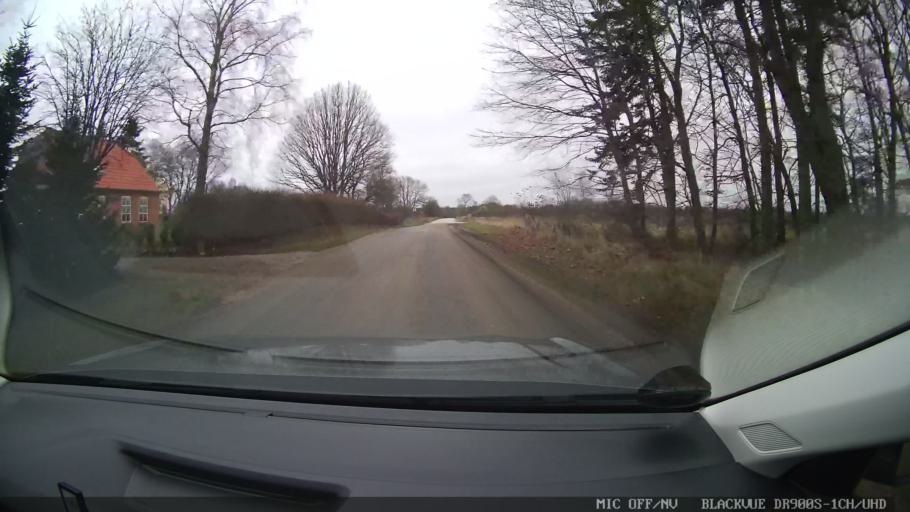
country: DK
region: Central Jutland
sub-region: Viborg Kommune
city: Viborg
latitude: 56.4188
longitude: 9.3811
